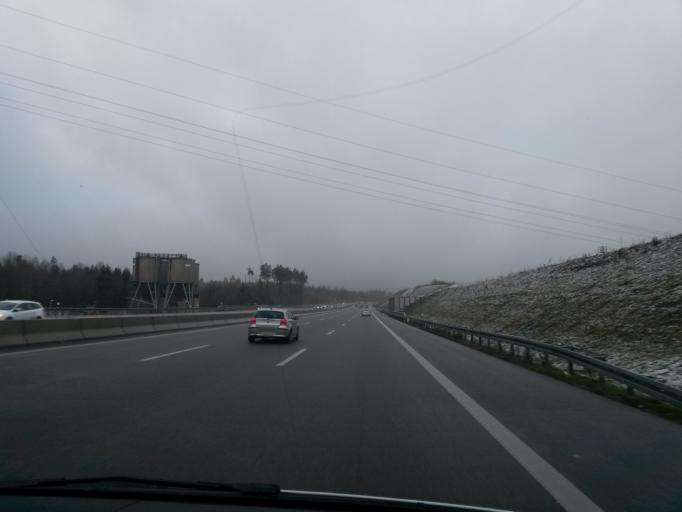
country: DE
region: Baden-Wuerttemberg
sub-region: Karlsruhe Region
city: Wimsheim
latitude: 48.8428
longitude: 8.8196
